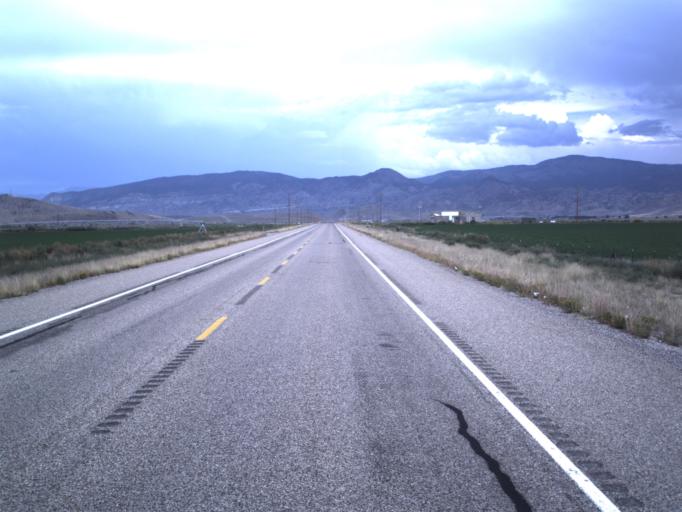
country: US
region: Utah
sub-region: Piute County
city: Junction
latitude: 38.1747
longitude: -112.2564
